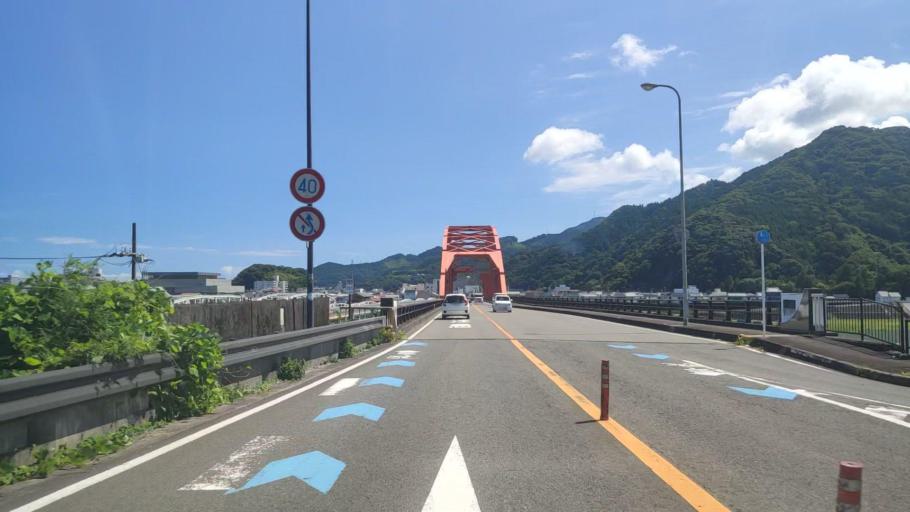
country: JP
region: Wakayama
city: Shingu
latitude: 33.7351
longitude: 135.9882
